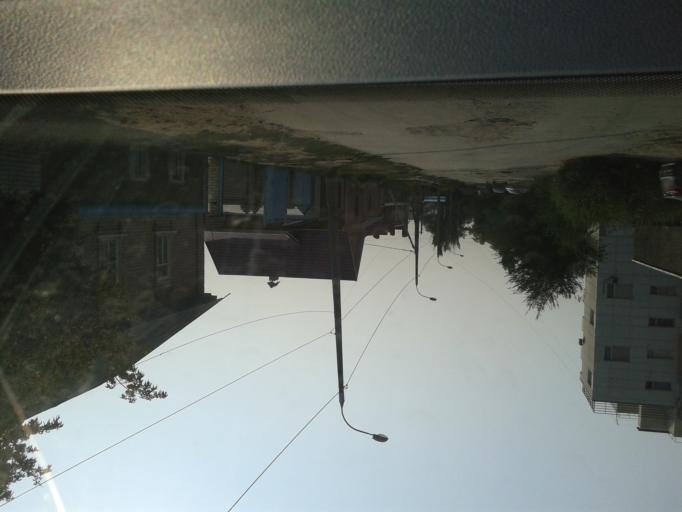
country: RU
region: Volgograd
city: Gorodishche
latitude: 48.7656
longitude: 44.4898
